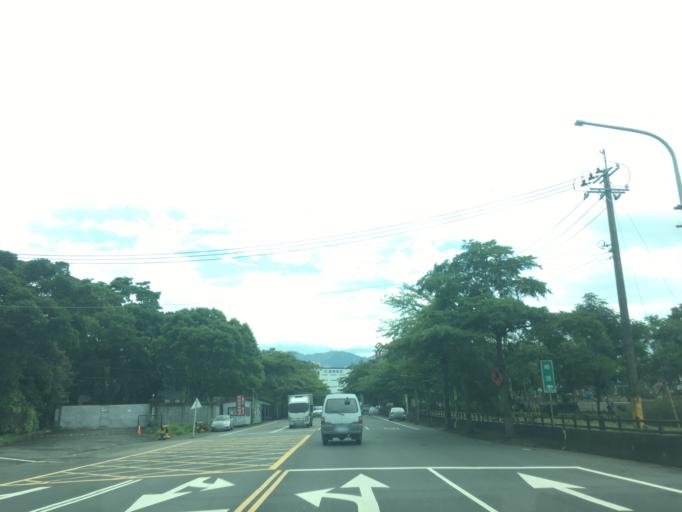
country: TW
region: Taiwan
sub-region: Yunlin
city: Douliu
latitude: 23.5946
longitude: 120.5254
